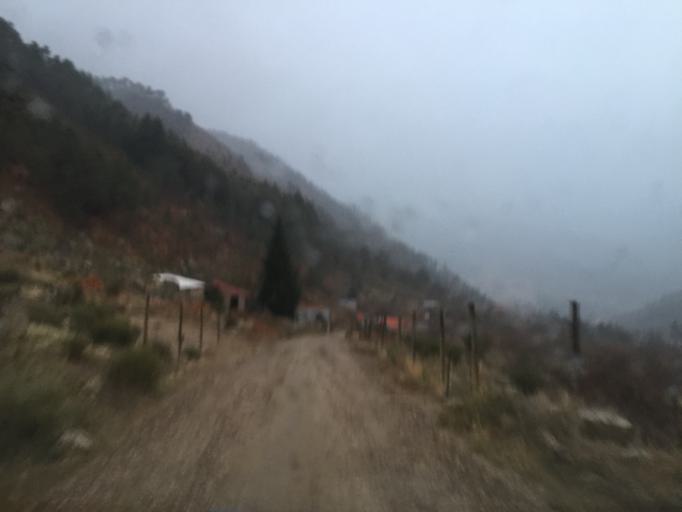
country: PT
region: Guarda
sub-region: Manteigas
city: Manteigas
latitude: 40.3758
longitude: -7.5504
